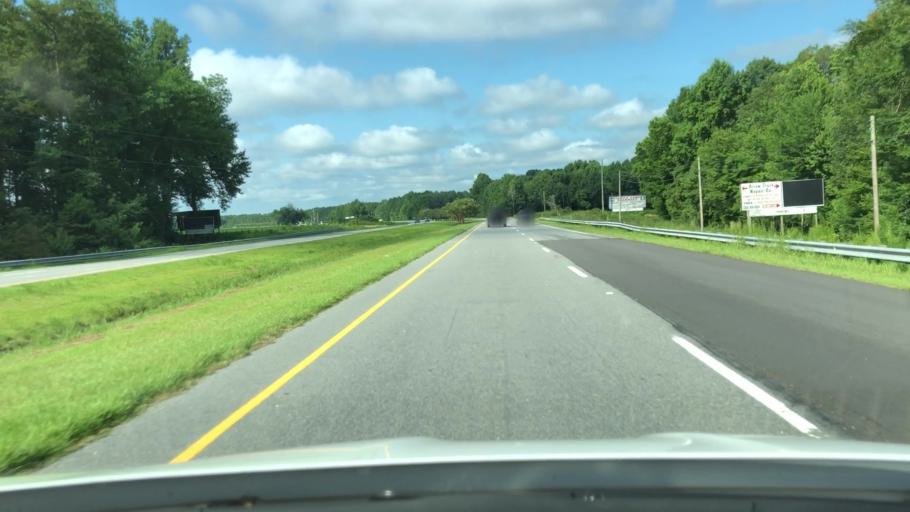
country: US
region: North Carolina
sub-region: Perquimans County
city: Hertford
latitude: 36.2092
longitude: -76.4414
